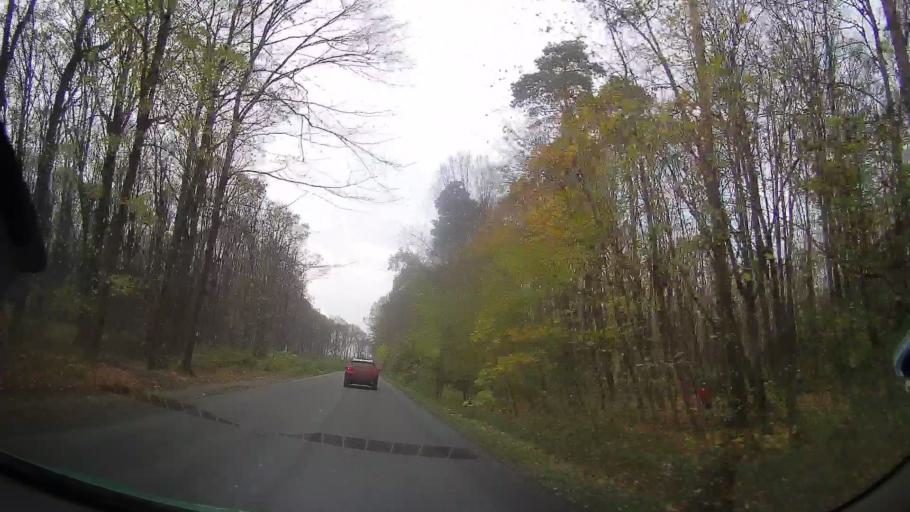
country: RO
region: Prahova
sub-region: Comuna Gorgota
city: Potigrafu
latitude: 44.7677
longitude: 26.1130
